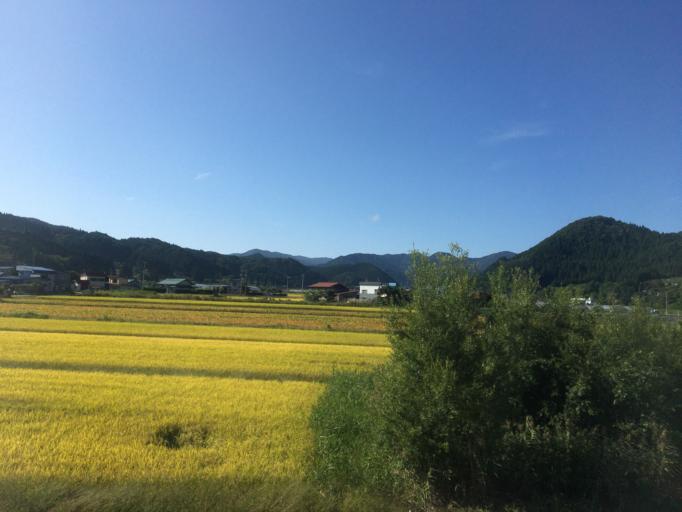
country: JP
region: Aomori
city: Hirosaki
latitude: 40.5257
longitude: 140.5521
